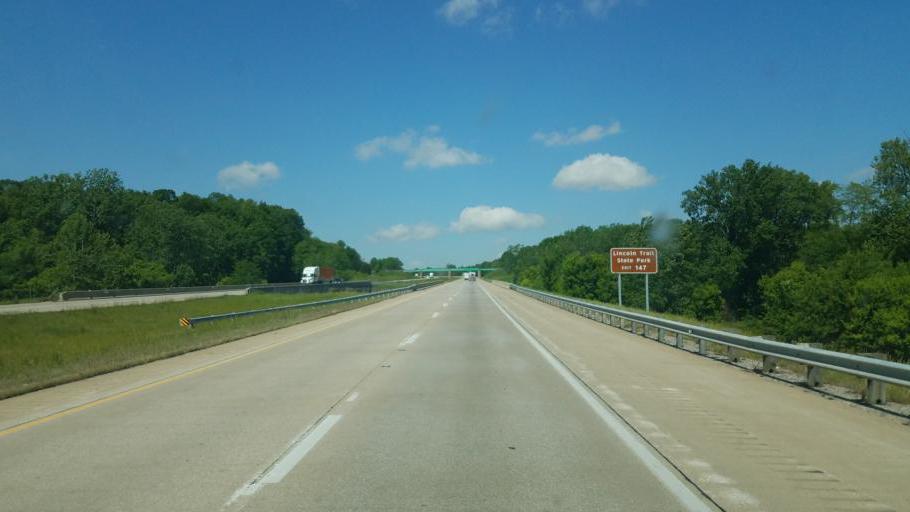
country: US
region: Illinois
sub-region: Clark County
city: Marshall
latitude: 39.4226
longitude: -87.6718
